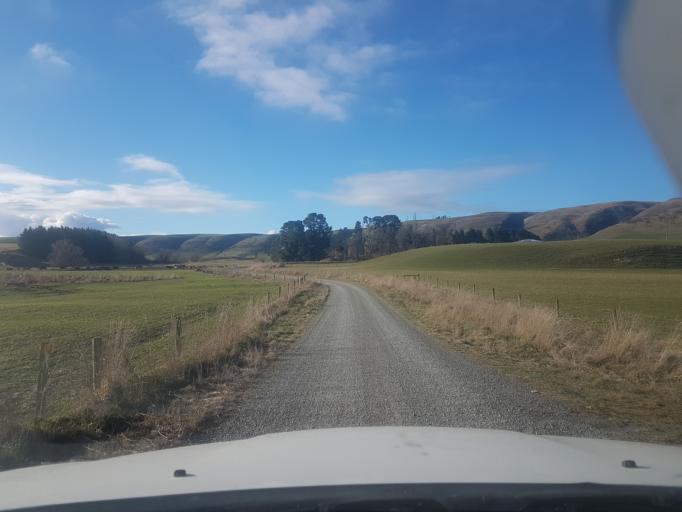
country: NZ
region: Canterbury
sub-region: Timaru District
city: Pleasant Point
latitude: -44.1766
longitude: 170.8607
